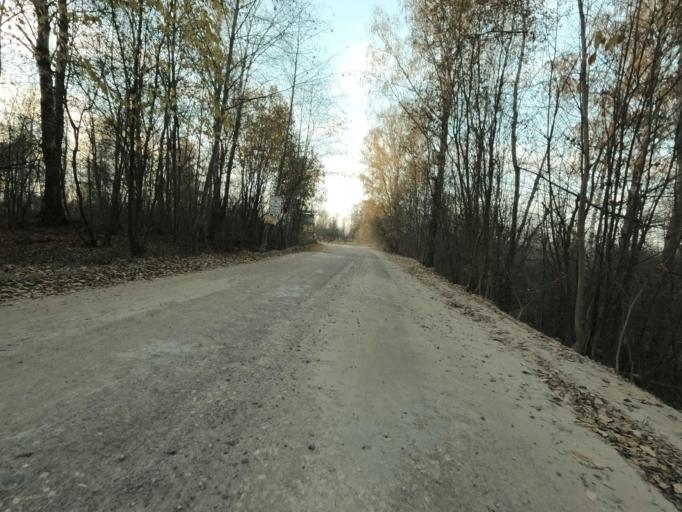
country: RU
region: Leningrad
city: Mga
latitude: 59.7737
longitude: 31.2258
